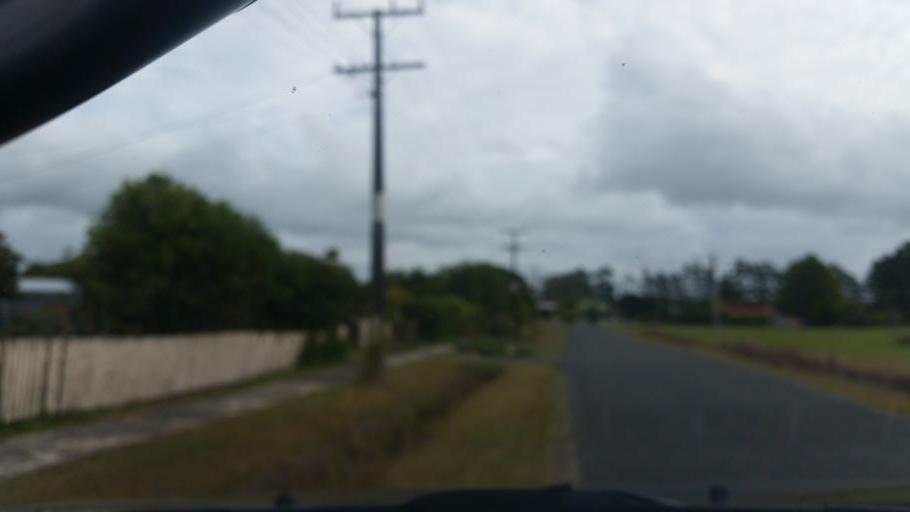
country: NZ
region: Northland
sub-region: Kaipara District
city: Dargaville
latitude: -36.0290
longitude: 173.9180
